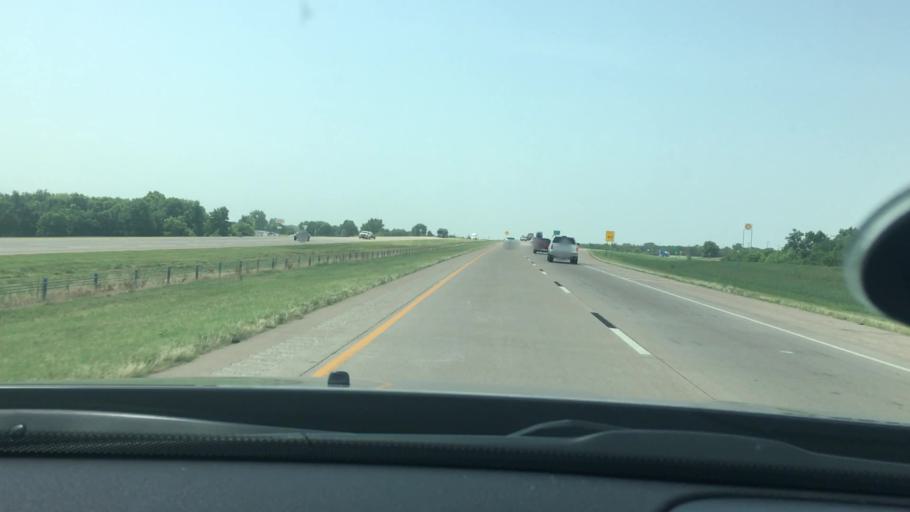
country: US
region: Oklahoma
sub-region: Garvin County
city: Wynnewood
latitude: 34.6567
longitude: -97.2210
